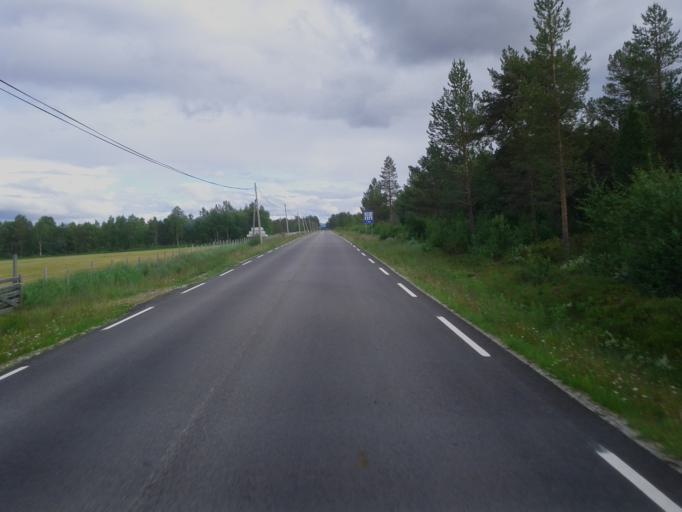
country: NO
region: Sor-Trondelag
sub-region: Roros
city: Roros
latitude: 62.2948
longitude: 11.7275
